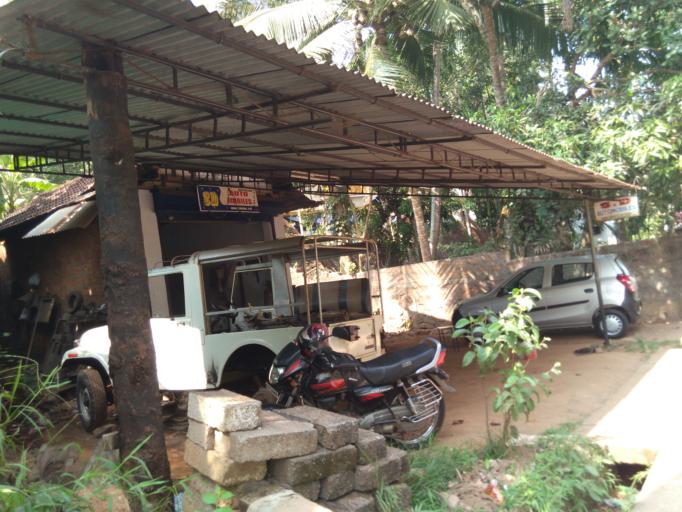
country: IN
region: Kerala
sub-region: Kozhikode
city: Kunnamangalam
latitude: 11.2956
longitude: 75.8356
